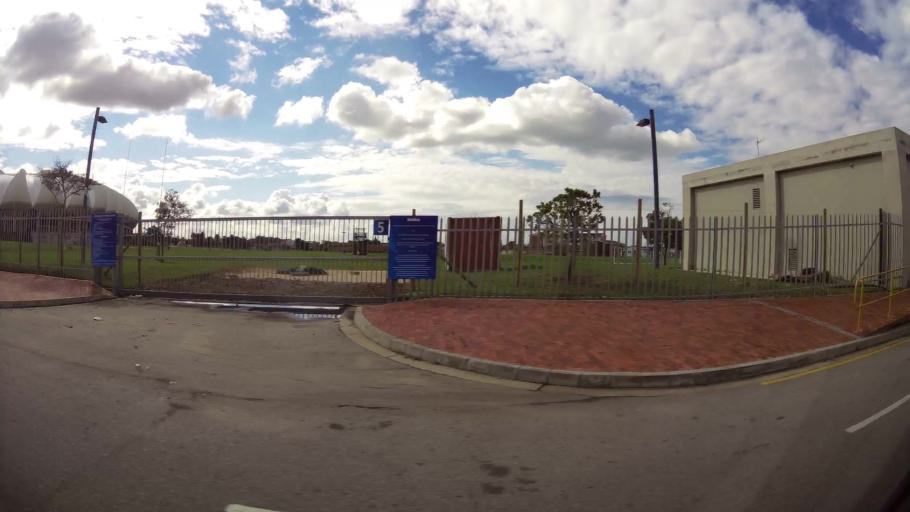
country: ZA
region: Eastern Cape
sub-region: Nelson Mandela Bay Metropolitan Municipality
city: Port Elizabeth
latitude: -33.9411
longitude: 25.6005
